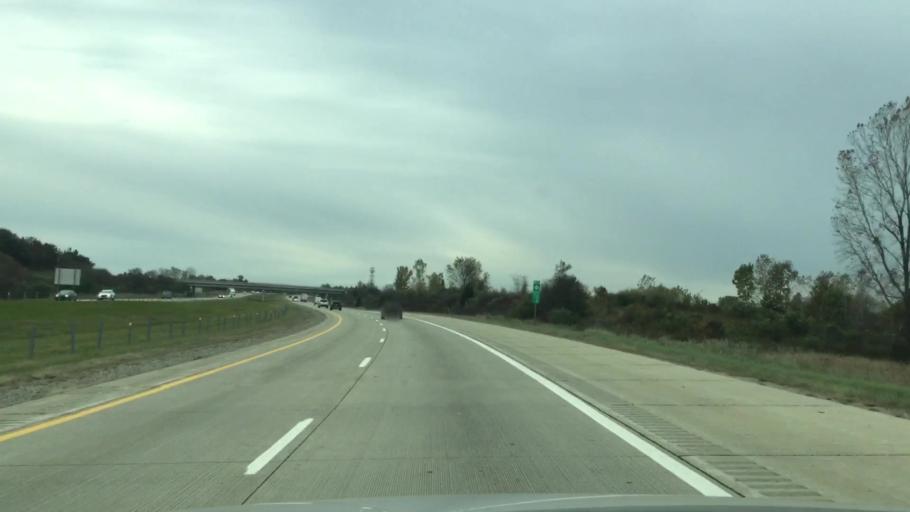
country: US
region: Michigan
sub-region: Wayne County
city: Plymouth
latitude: 42.3792
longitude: -83.5315
